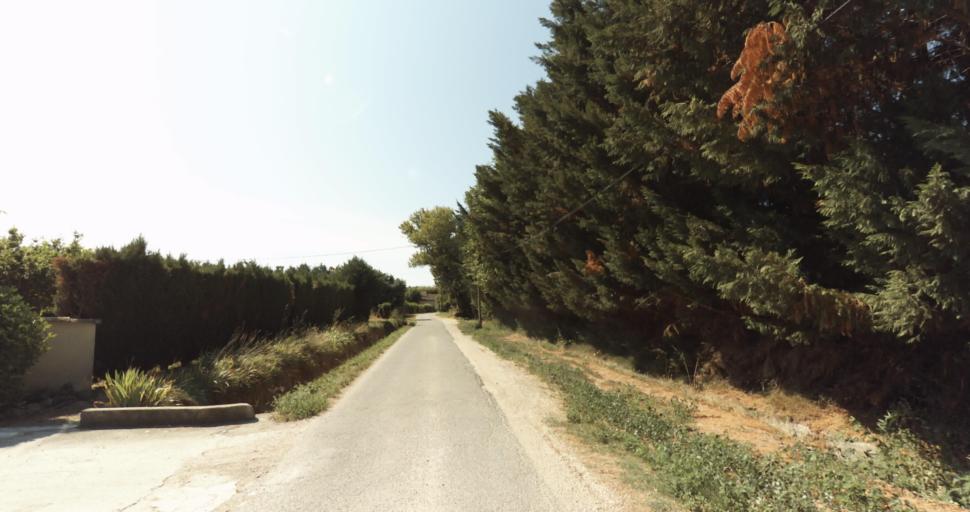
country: FR
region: Provence-Alpes-Cote d'Azur
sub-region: Departement du Vaucluse
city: Monteux
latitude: 44.0139
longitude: 4.9944
